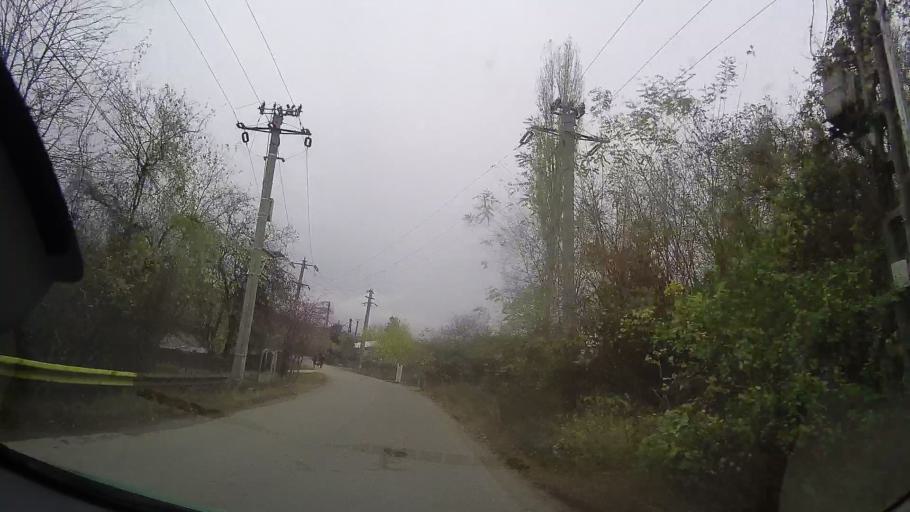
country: RO
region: Prahova
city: Ceptura de Sus
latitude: 45.0502
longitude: 26.2989
